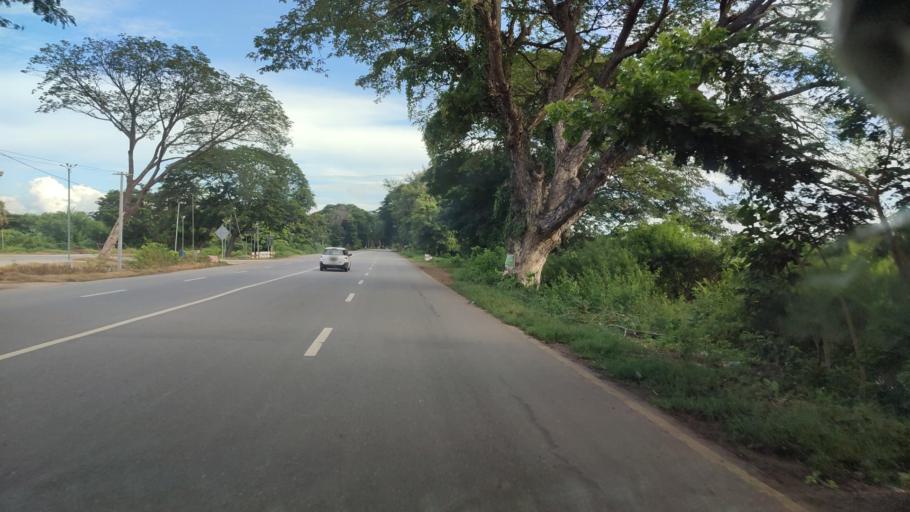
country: MM
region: Mandalay
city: Yamethin
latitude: 20.2181
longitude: 96.1818
